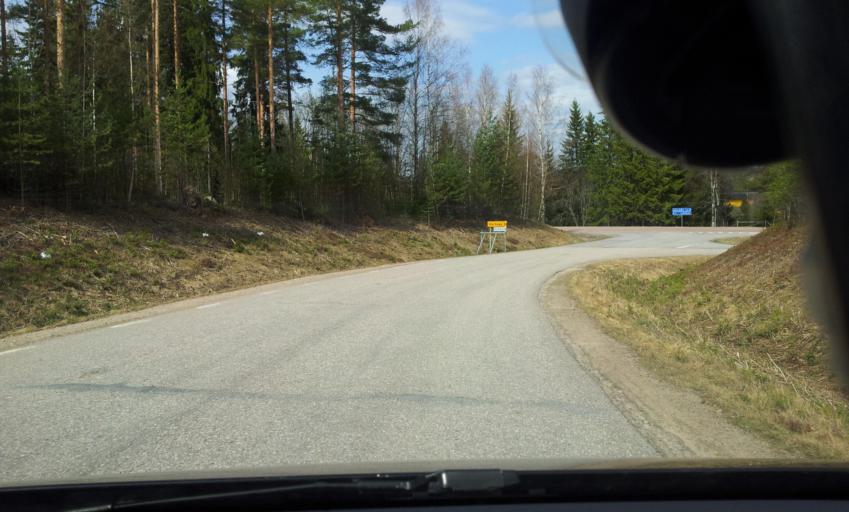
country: SE
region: Gaevleborg
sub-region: Ljusdals Kommun
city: Ljusdal
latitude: 61.8149
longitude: 16.0780
